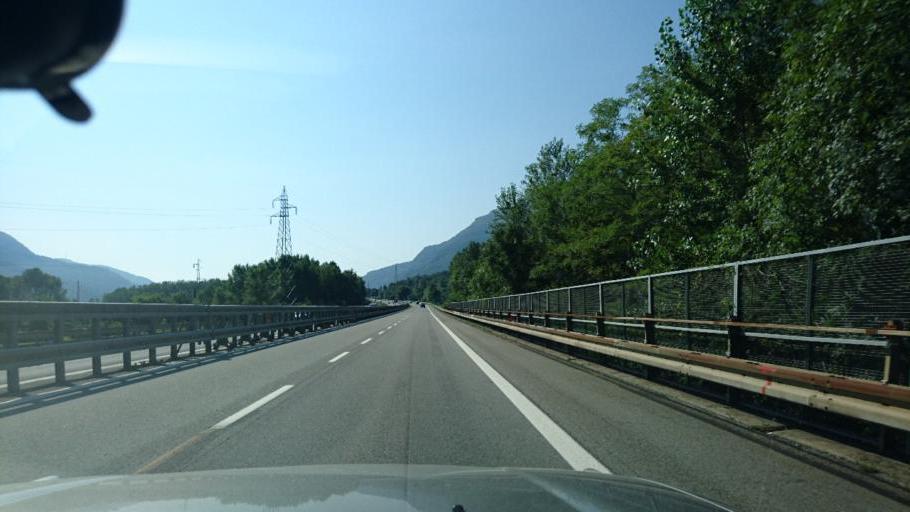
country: IT
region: Piedmont
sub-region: Provincia di Torino
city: Carema
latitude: 45.5746
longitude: 7.8028
